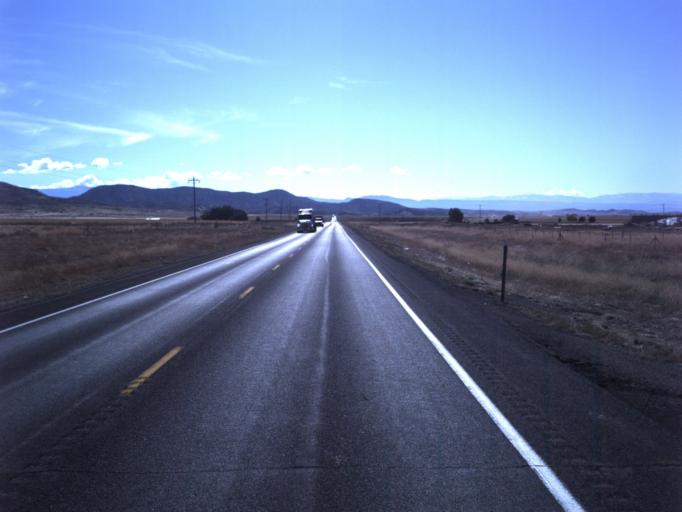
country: US
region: Utah
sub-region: Sanpete County
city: Gunnison
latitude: 39.2669
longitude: -111.8696
